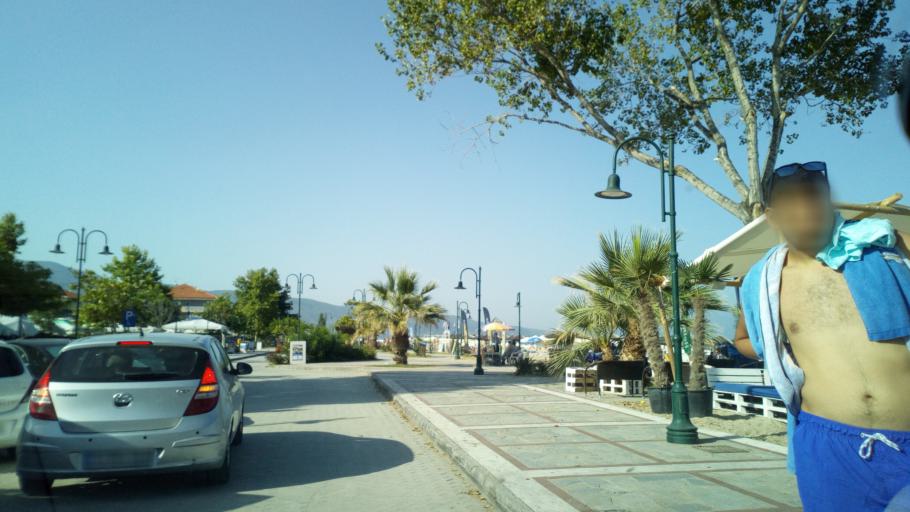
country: GR
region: Central Macedonia
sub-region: Nomos Thessalonikis
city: Nea Vrasna
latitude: 40.7074
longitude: 23.7023
